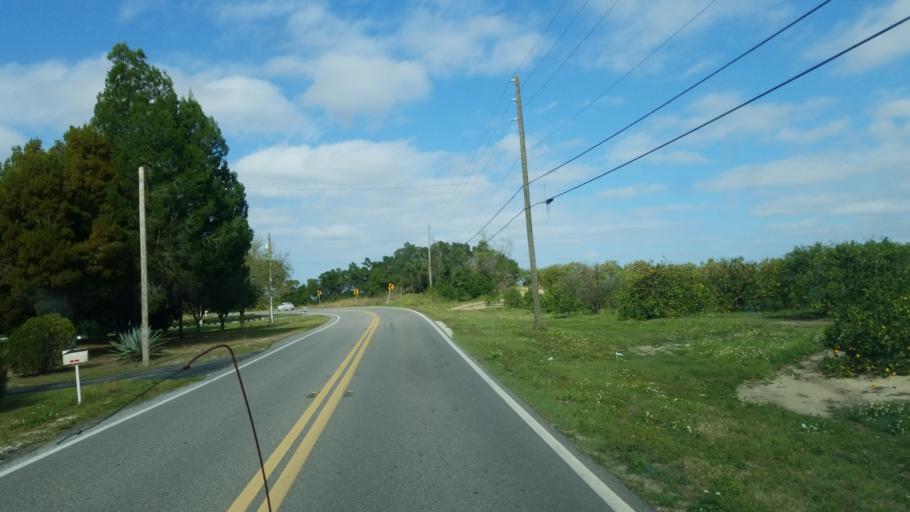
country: US
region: Florida
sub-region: Polk County
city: Lake Wales
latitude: 27.9622
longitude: -81.5817
